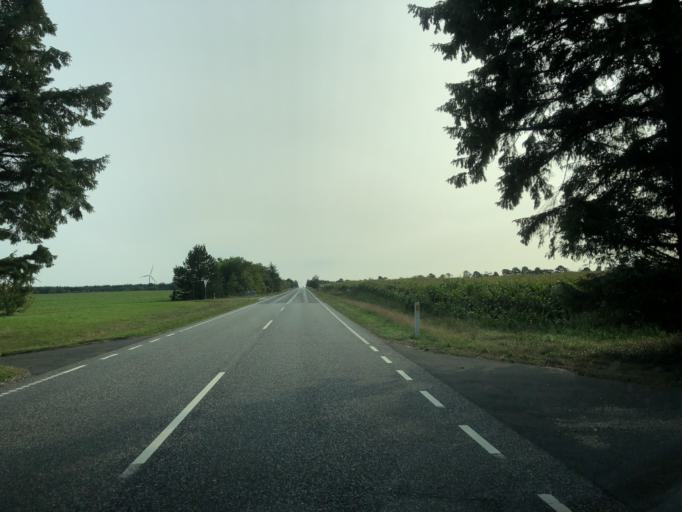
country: DK
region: Central Jutland
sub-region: Ringkobing-Skjern Kommune
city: Videbaek
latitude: 56.1636
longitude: 8.6784
